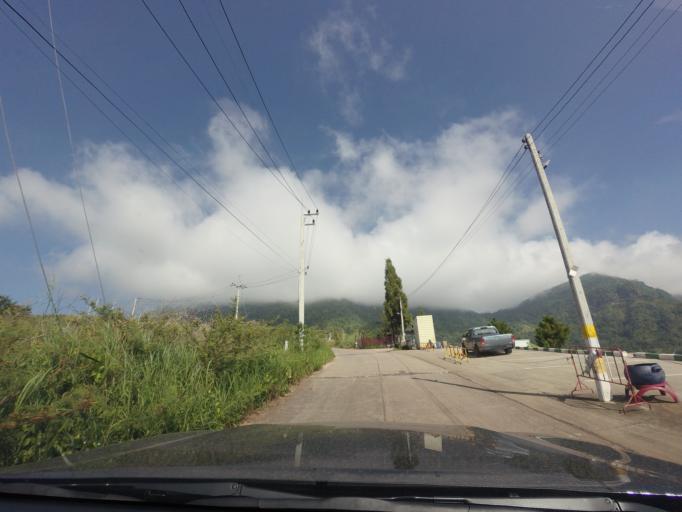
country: TH
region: Phetchabun
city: Khao Kho
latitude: 16.7939
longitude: 101.0434
